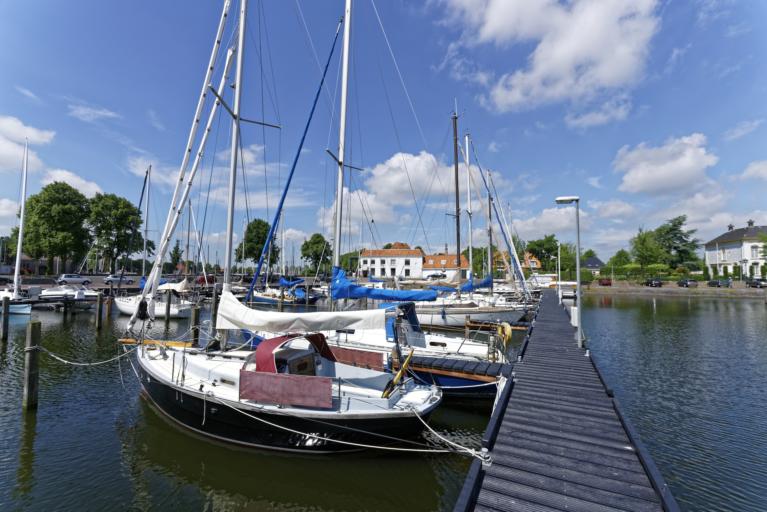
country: NL
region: North Holland
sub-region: Gemeente Medemblik
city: Medemblik
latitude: 52.7698
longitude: 5.1100
